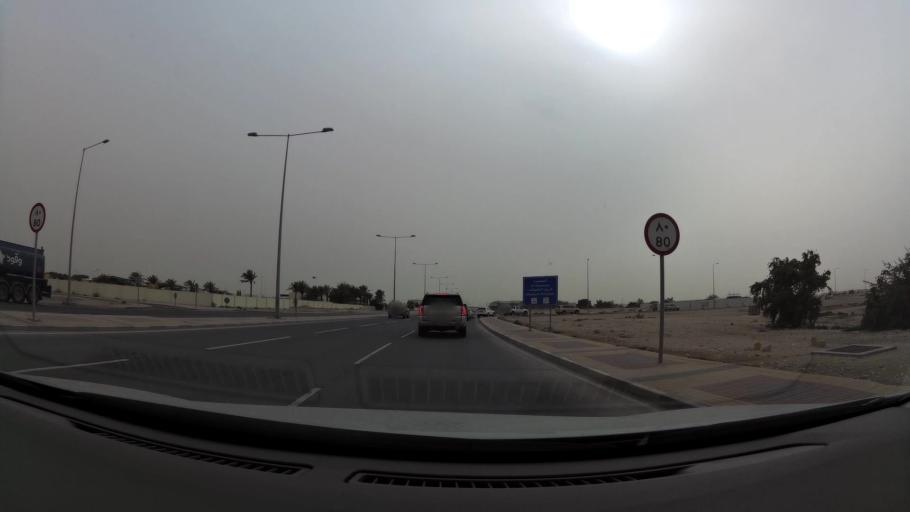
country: QA
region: Baladiyat ad Dawhah
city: Doha
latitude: 25.2400
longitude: 51.5176
